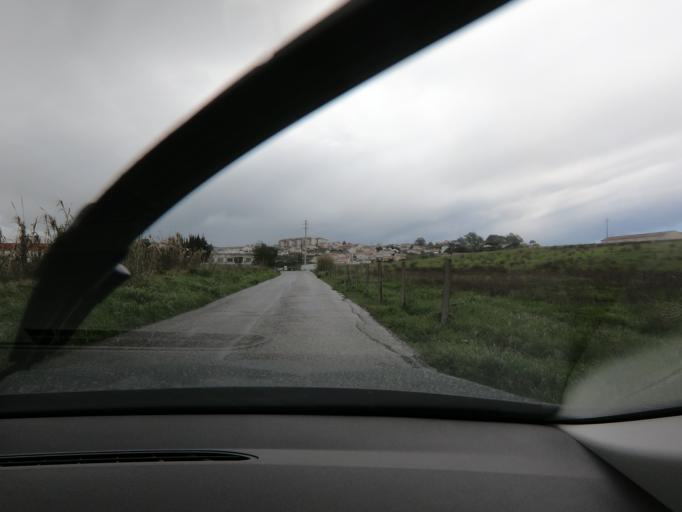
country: PT
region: Lisbon
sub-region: Alenquer
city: Carregado
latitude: 39.0239
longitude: -8.9883
